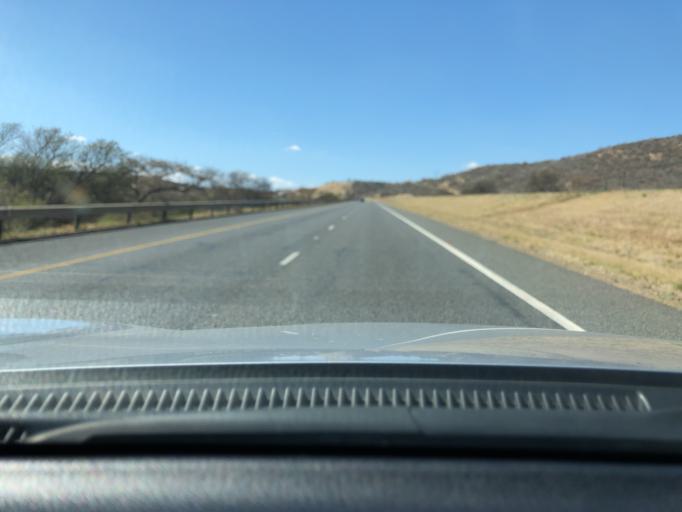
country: ZA
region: KwaZulu-Natal
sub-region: uThukela District Municipality
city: Estcourt
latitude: -29.0420
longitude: 29.8612
